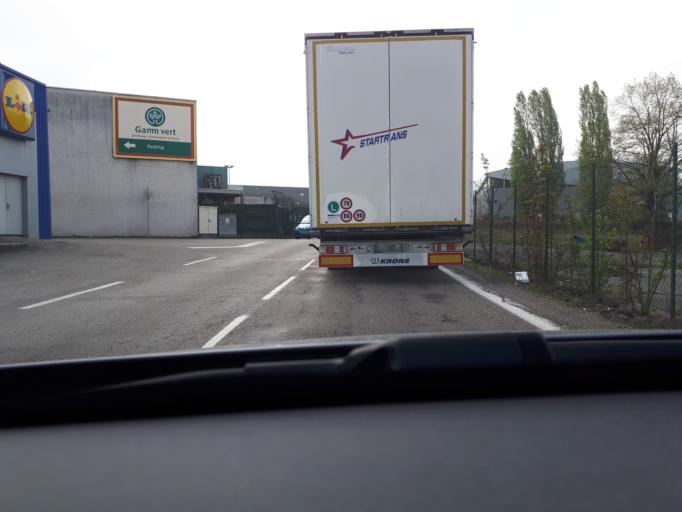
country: FR
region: Rhone-Alpes
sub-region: Departement de l'Isere
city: Bourgoin-Jallieu
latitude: 45.5969
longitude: 5.2658
